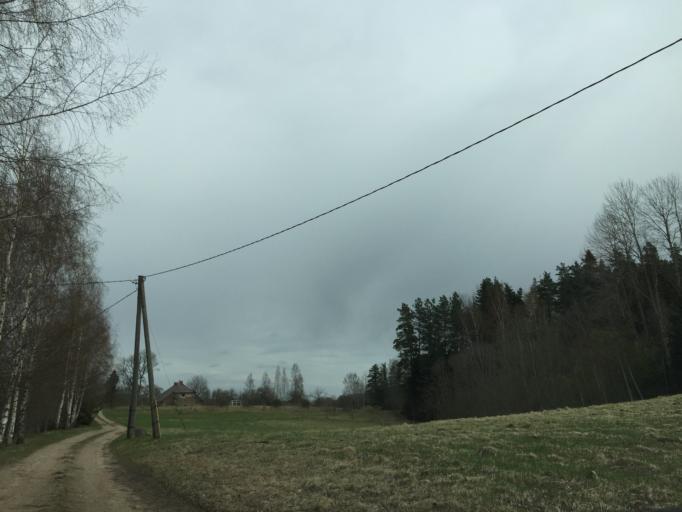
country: LV
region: Priekuli
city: Priekuli
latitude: 57.2915
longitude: 25.3283
